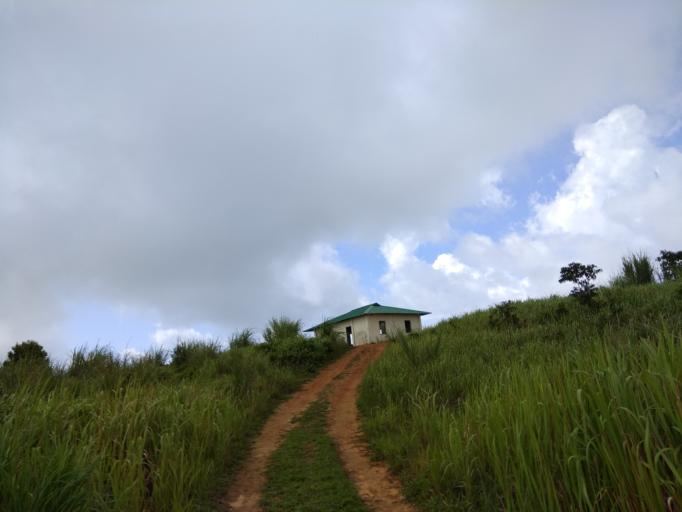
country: BD
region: Chittagong
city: Bandarban
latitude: 21.7439
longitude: 92.4178
